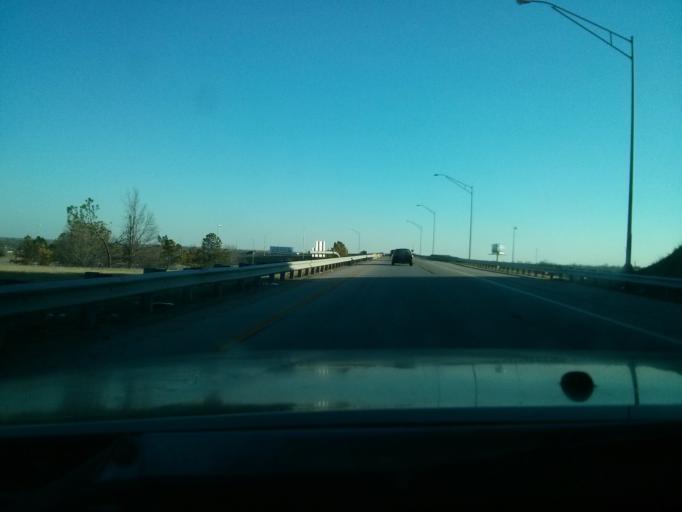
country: US
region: Oklahoma
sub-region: Tulsa County
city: Owasso
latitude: 36.1639
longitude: -95.8826
